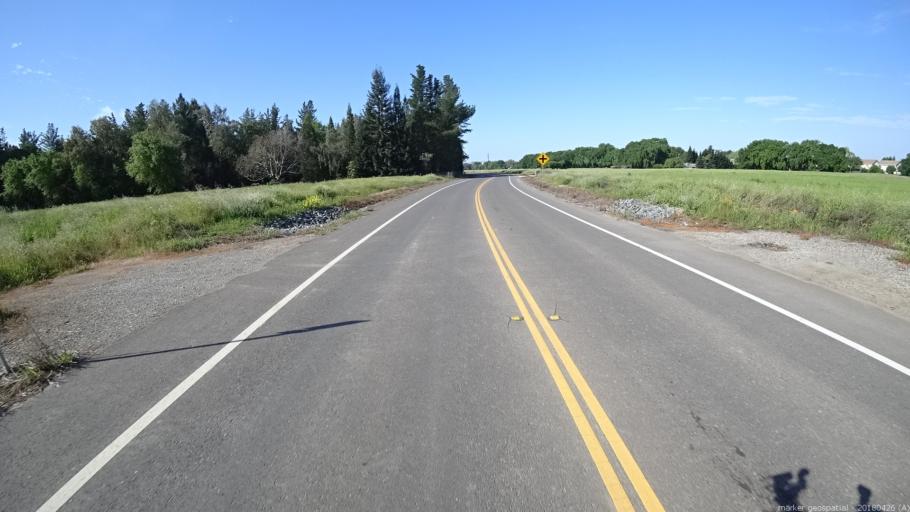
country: US
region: California
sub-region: Yolo County
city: West Sacramento
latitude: 38.5443
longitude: -121.5179
